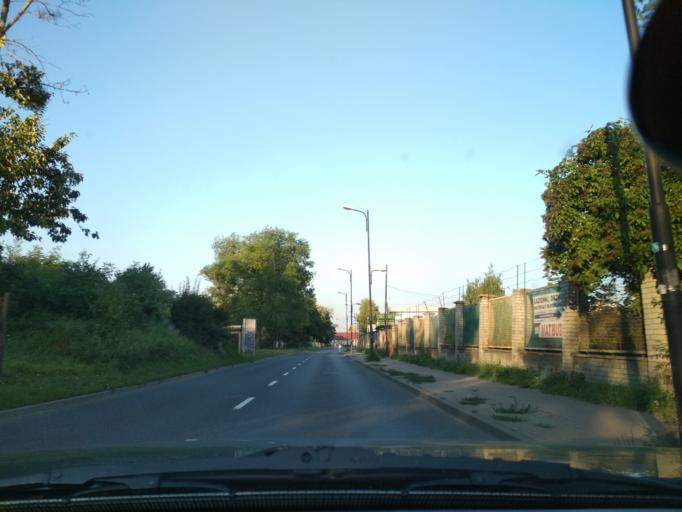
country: PL
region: Silesian Voivodeship
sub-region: Gliwice
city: Gliwice
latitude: 50.2749
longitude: 18.6680
